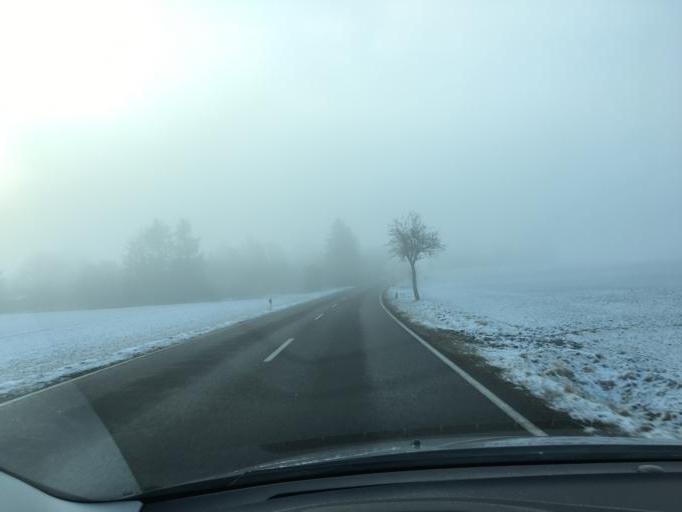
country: DE
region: Saxony
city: Narsdorf
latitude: 51.0208
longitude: 12.7310
